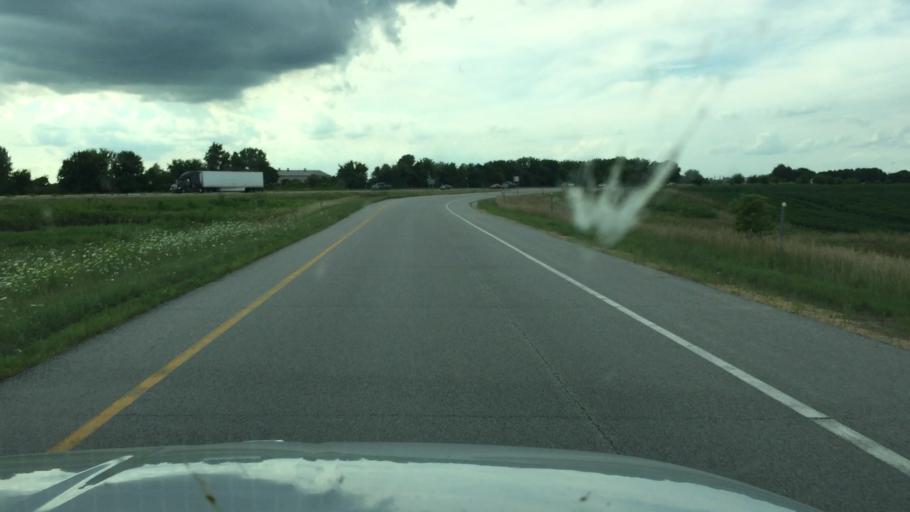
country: US
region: Iowa
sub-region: Scott County
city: Blue Grass
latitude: 41.5401
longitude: -90.6760
